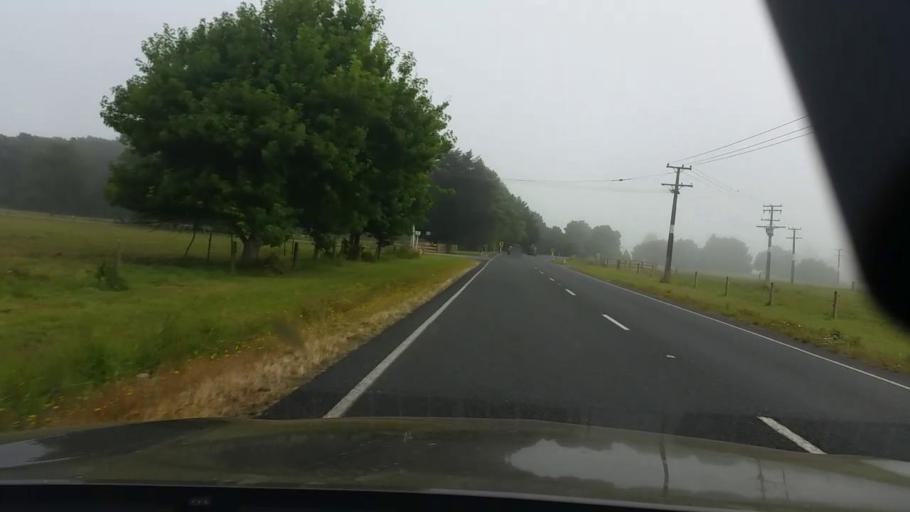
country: NZ
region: Waikato
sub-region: Hamilton City
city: Hamilton
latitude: -37.6425
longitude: 175.2950
